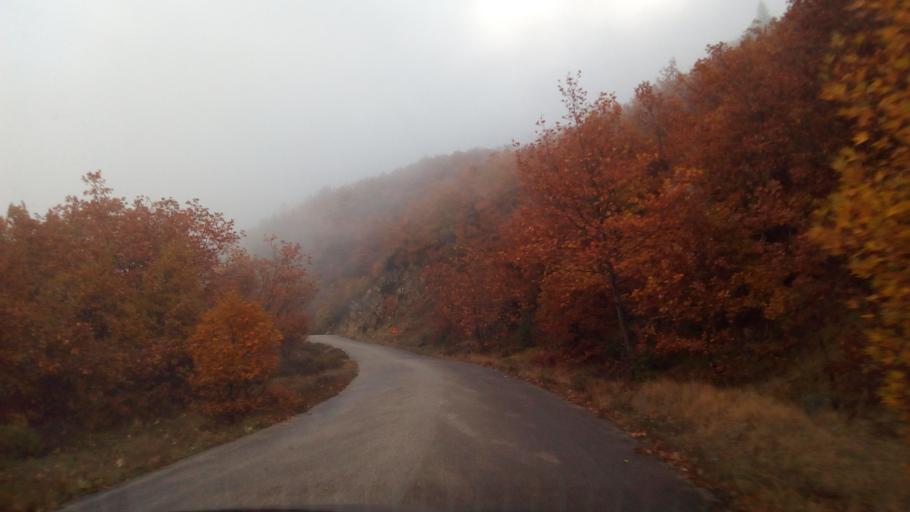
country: GR
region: West Greece
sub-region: Nomos Aitolias kai Akarnanias
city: Nafpaktos
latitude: 38.5518
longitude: 21.9287
